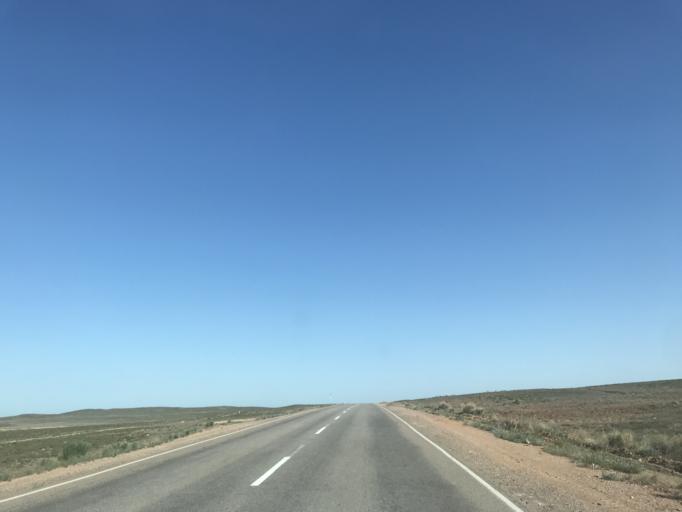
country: KZ
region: Zhambyl
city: Mynaral
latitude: 45.4908
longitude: 73.5291
